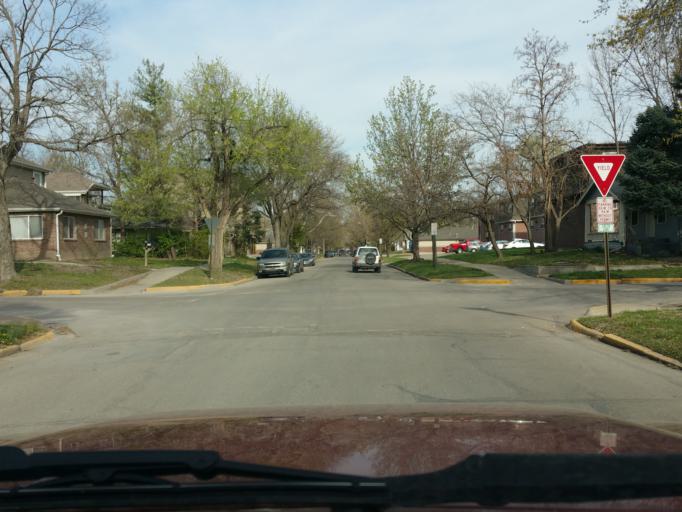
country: US
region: Kansas
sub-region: Riley County
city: Manhattan
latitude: 39.1879
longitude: -96.5718
